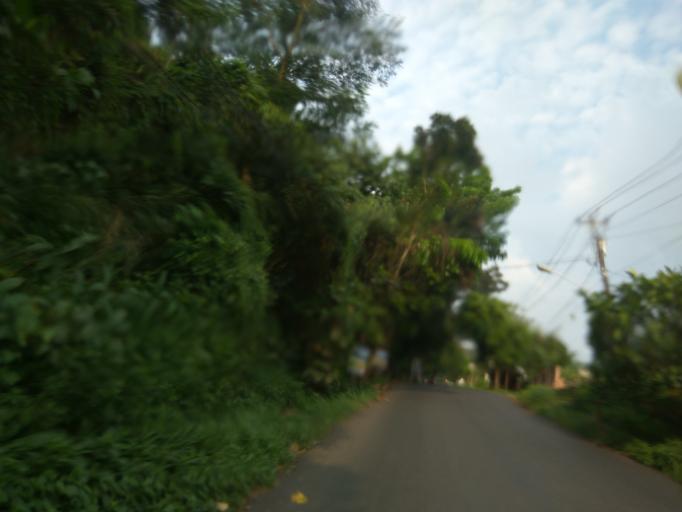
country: ID
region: Central Java
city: Semarang
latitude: -7.0235
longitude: 110.4015
